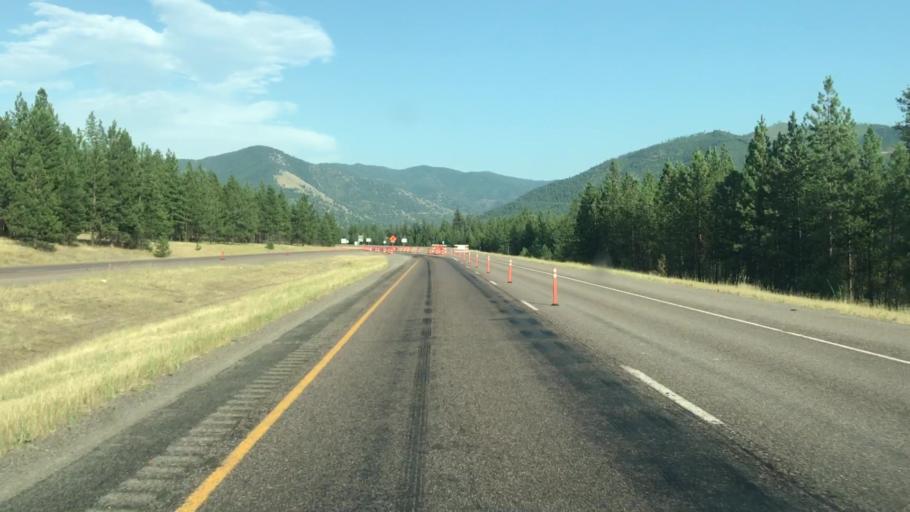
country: US
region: Montana
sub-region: Mineral County
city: Superior
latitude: 47.0141
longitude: -114.7305
